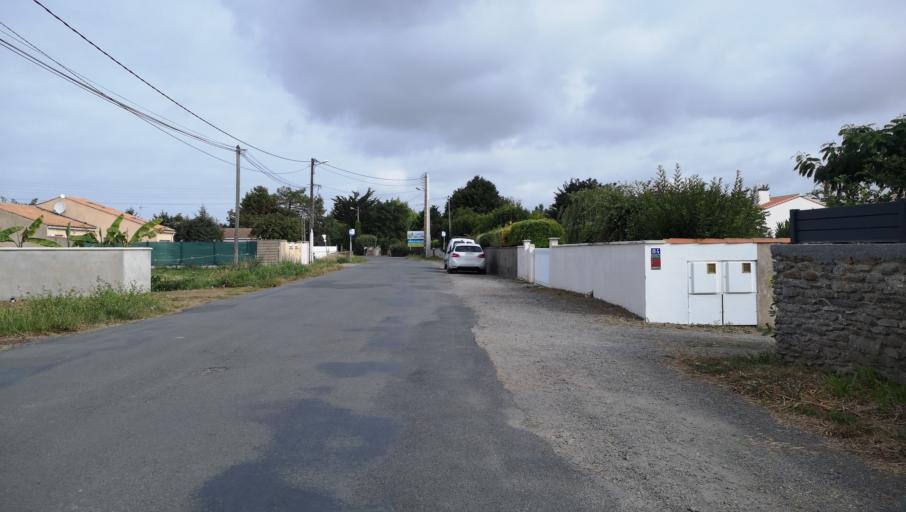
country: FR
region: Pays de la Loire
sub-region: Departement de la Vendee
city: Olonne-sur-Mer
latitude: 46.5535
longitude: -1.8051
